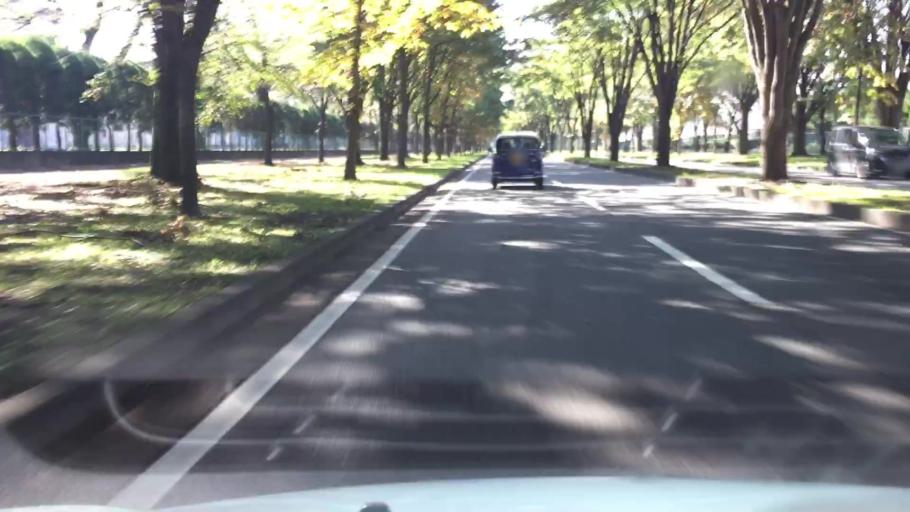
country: JP
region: Tochigi
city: Utsunomiya-shi
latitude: 36.5423
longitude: 139.9866
